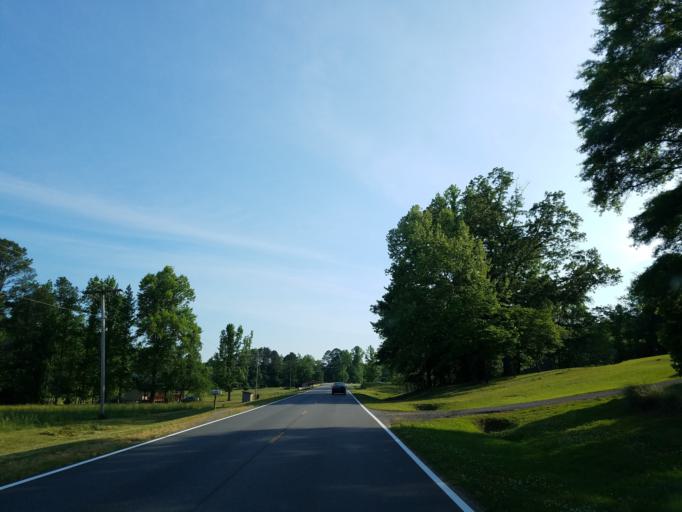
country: US
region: Georgia
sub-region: Chattooga County
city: Trion
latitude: 34.5559
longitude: -85.1904
